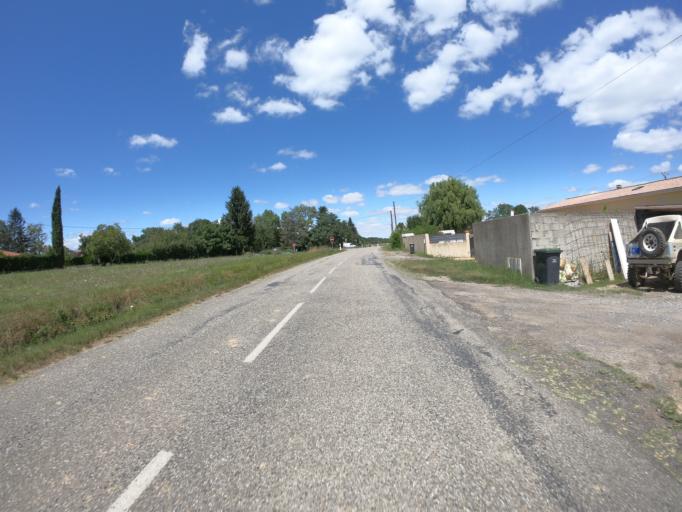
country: FR
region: Midi-Pyrenees
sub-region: Departement de l'Ariege
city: Verniolle
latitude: 43.0650
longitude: 1.7384
